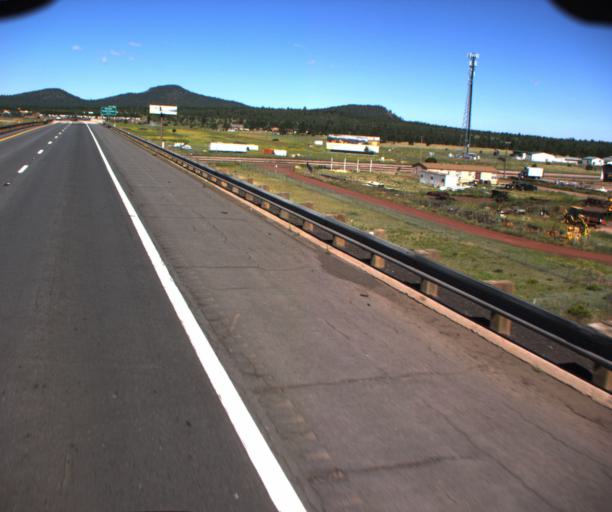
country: US
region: Arizona
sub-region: Coconino County
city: Williams
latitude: 35.2641
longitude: -112.1774
